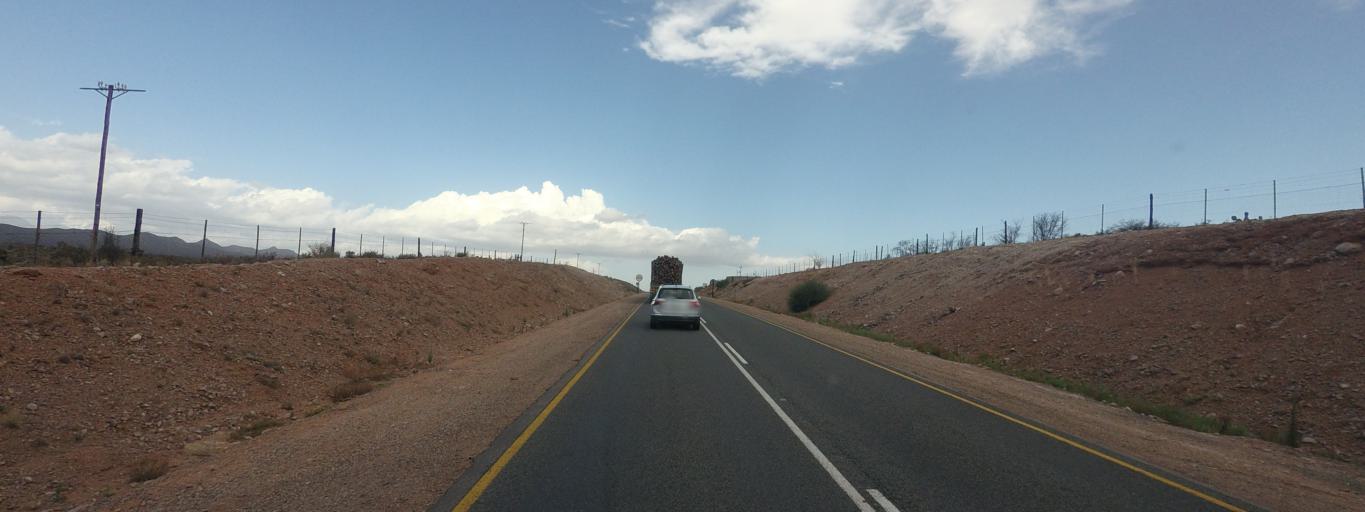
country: ZA
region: Western Cape
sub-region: Eden District Municipality
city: Ladismith
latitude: -33.5322
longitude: 21.7007
